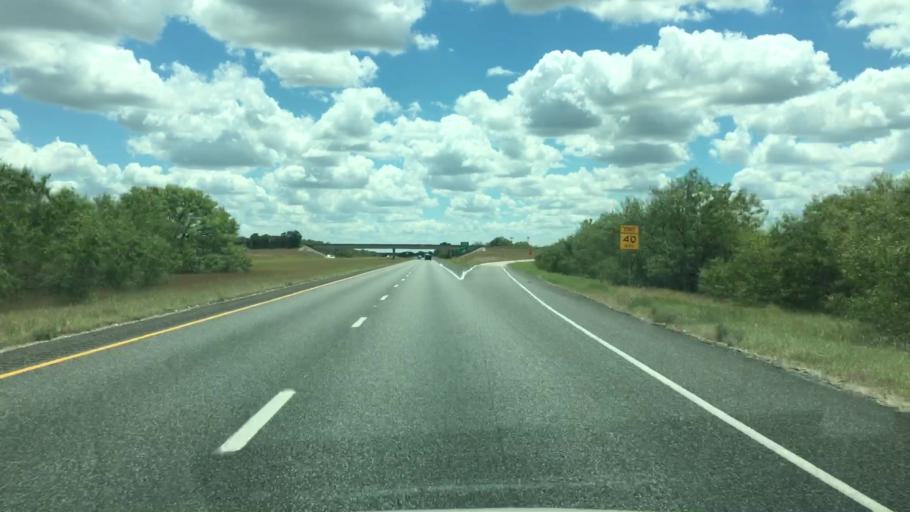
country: US
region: Texas
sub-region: Atascosa County
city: Pleasanton
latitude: 28.9204
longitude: -98.4352
